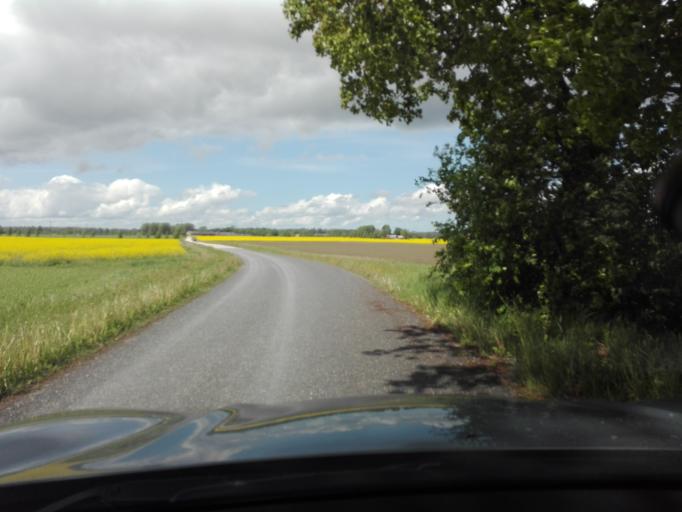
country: EE
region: Raplamaa
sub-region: Kehtna vald
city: Kehtna
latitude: 58.9635
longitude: 24.8898
